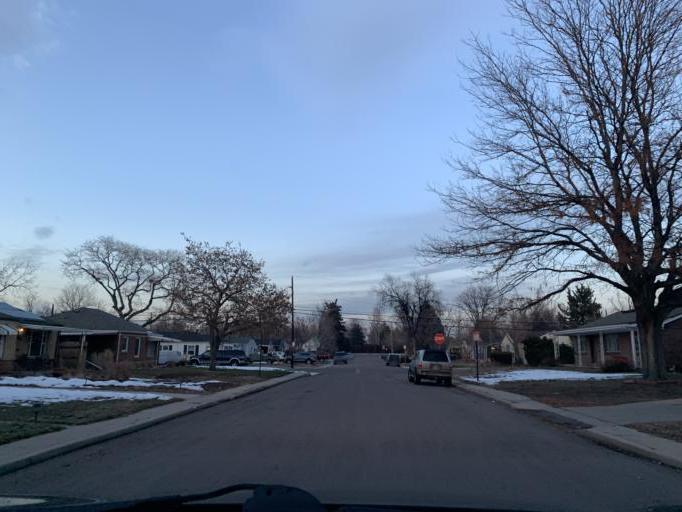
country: US
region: Colorado
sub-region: Adams County
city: Berkley
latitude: 39.7816
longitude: -105.0381
